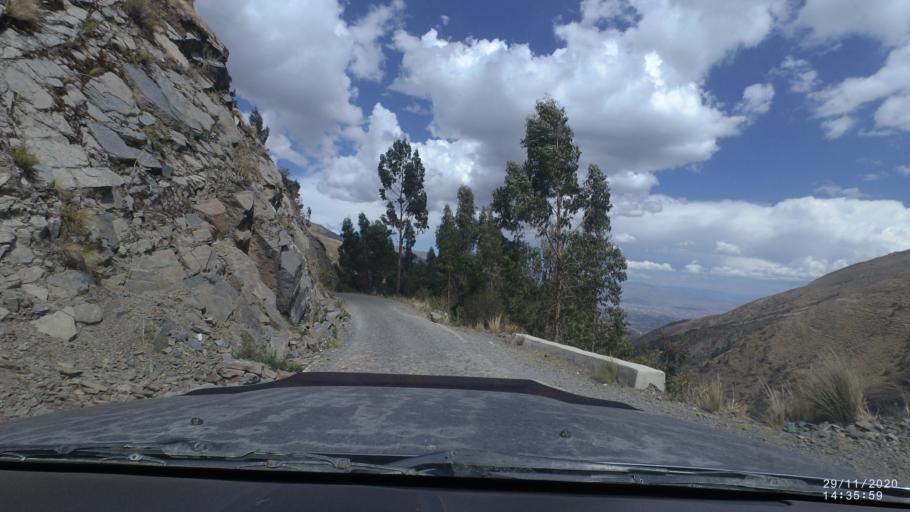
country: BO
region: Cochabamba
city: Sipe Sipe
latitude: -17.2719
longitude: -66.3329
